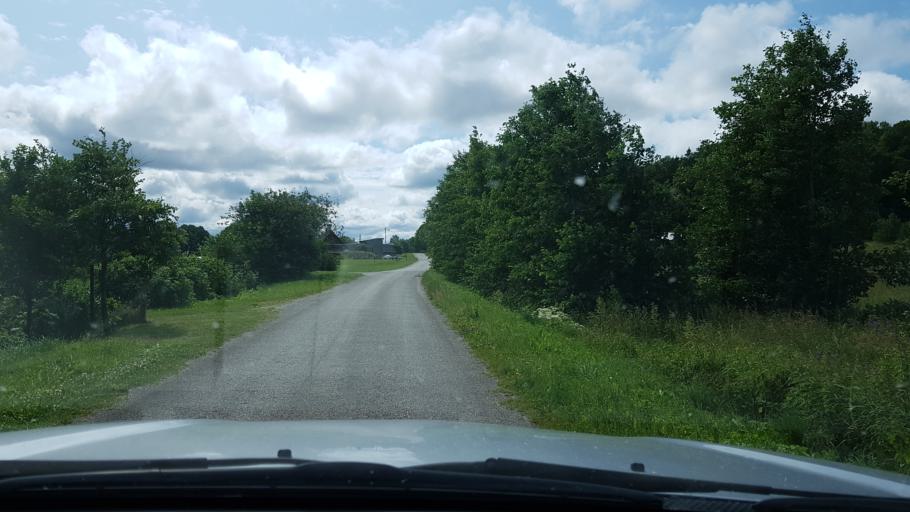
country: EE
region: Ida-Virumaa
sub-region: Sillamaee linn
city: Sillamae
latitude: 59.3763
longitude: 27.8709
